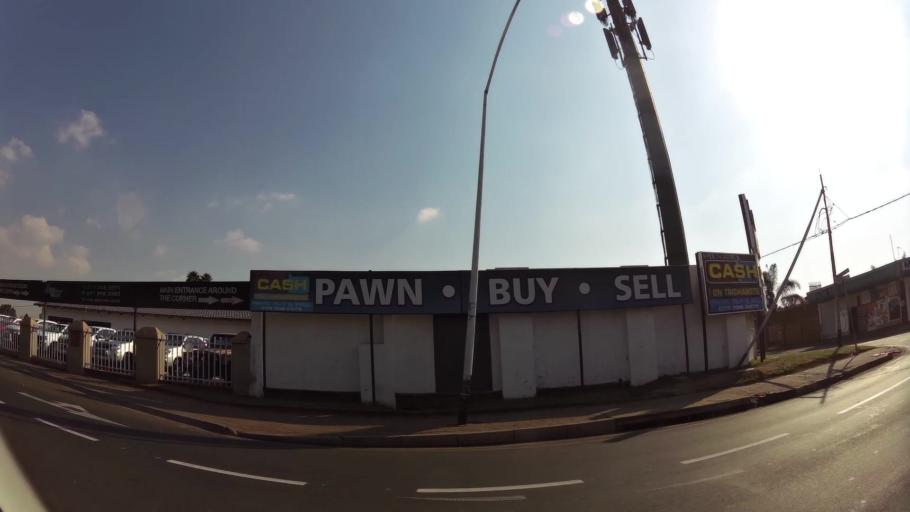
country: ZA
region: Gauteng
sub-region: Ekurhuleni Metropolitan Municipality
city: Boksburg
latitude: -26.1909
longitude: 28.2538
